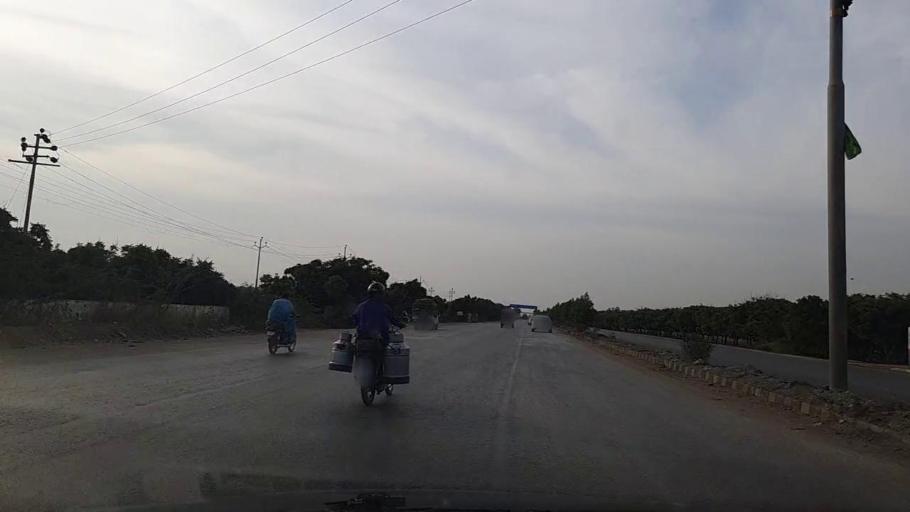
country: PK
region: Sindh
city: Gharo
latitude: 24.8511
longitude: 67.4222
